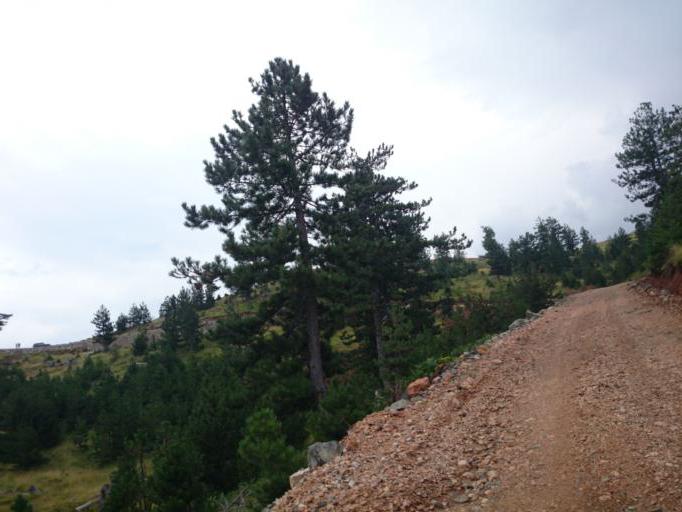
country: AL
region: Diber
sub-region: Rrethi i Dibres
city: Fushe-Lure
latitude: 41.7744
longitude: 20.2222
